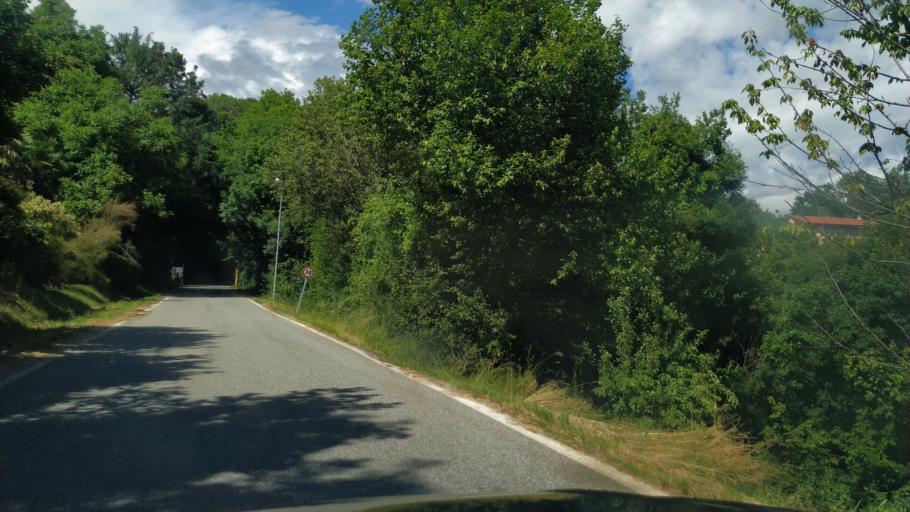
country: IT
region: Piedmont
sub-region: Provincia di Torino
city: Cintano
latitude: 45.4304
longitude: 7.6926
